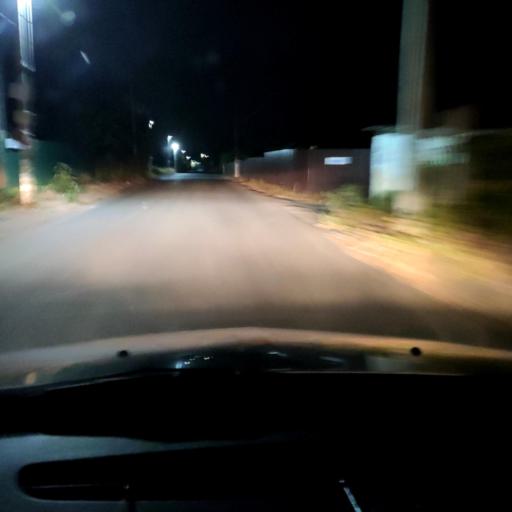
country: RU
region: Voronezj
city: Shilovo
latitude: 51.5925
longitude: 39.1572
